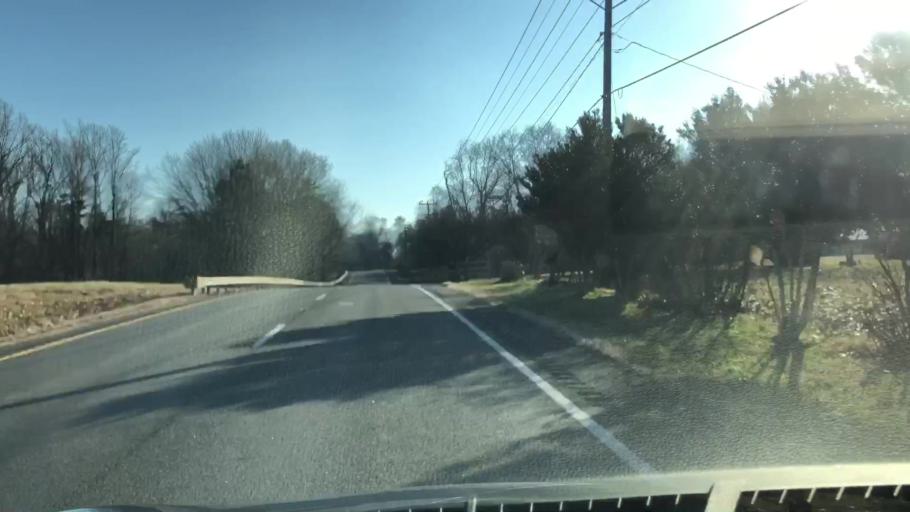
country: US
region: Virginia
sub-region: Fauquier County
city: Bealeton
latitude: 38.5873
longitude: -77.8023
